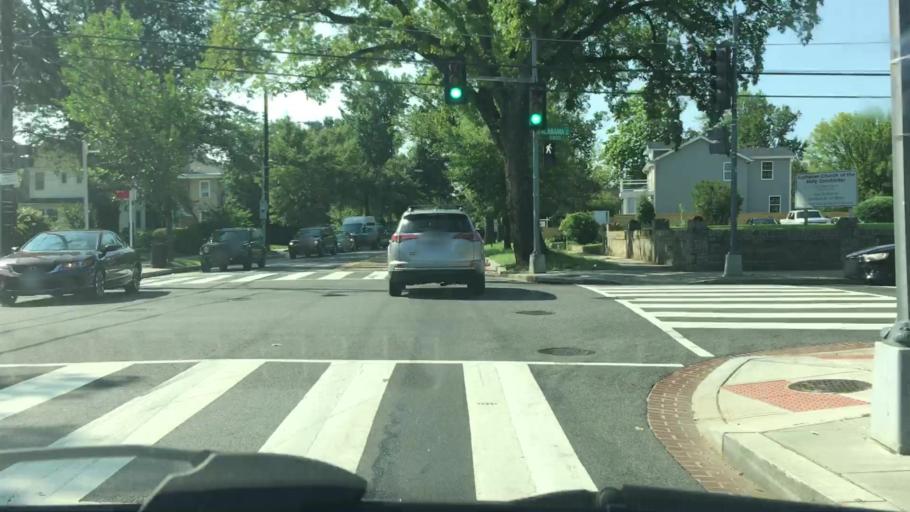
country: US
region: Maryland
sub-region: Prince George's County
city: Silver Hill
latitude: 38.8620
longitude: -76.9591
